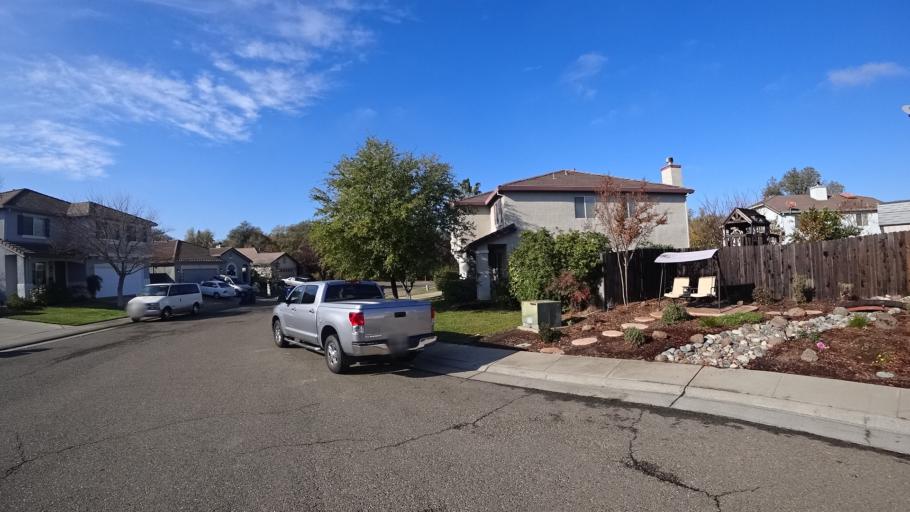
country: US
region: California
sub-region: Sacramento County
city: Antelope
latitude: 38.6910
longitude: -121.3117
